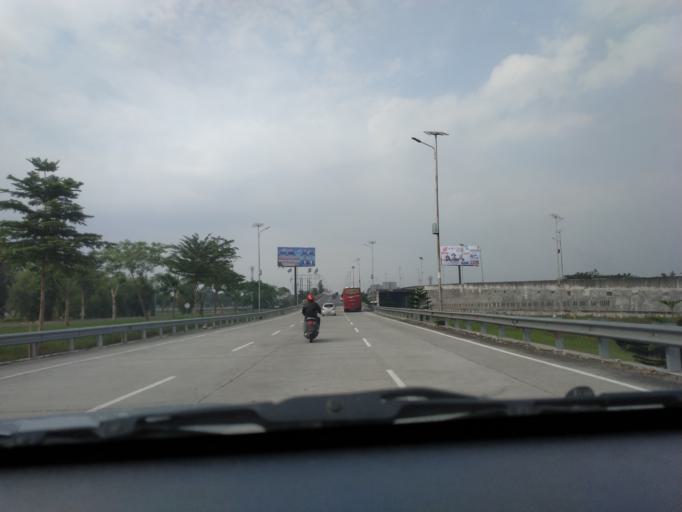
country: ID
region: North Sumatra
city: Percut
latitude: 3.6117
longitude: 98.8556
